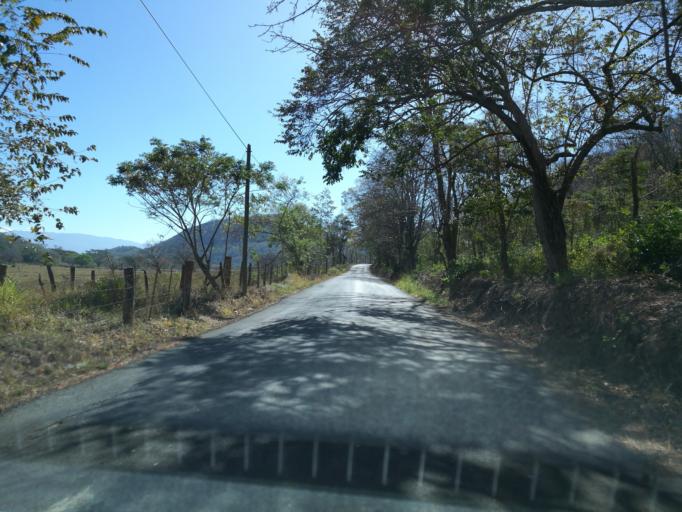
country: CR
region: Puntarenas
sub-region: Canton Central de Puntarenas
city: Puntarenas
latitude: 10.0868
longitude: -84.9335
